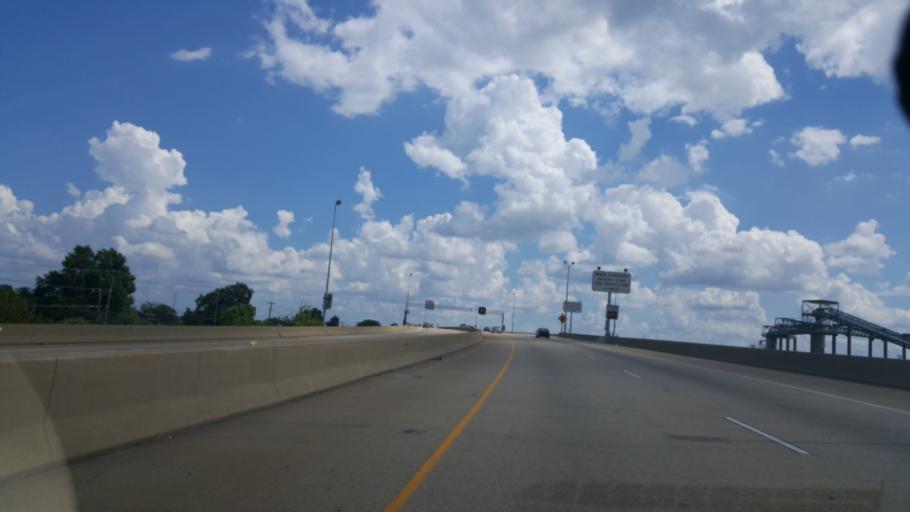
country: US
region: Virginia
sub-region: City of Newport News
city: Newport News
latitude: 36.9770
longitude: -76.4225
